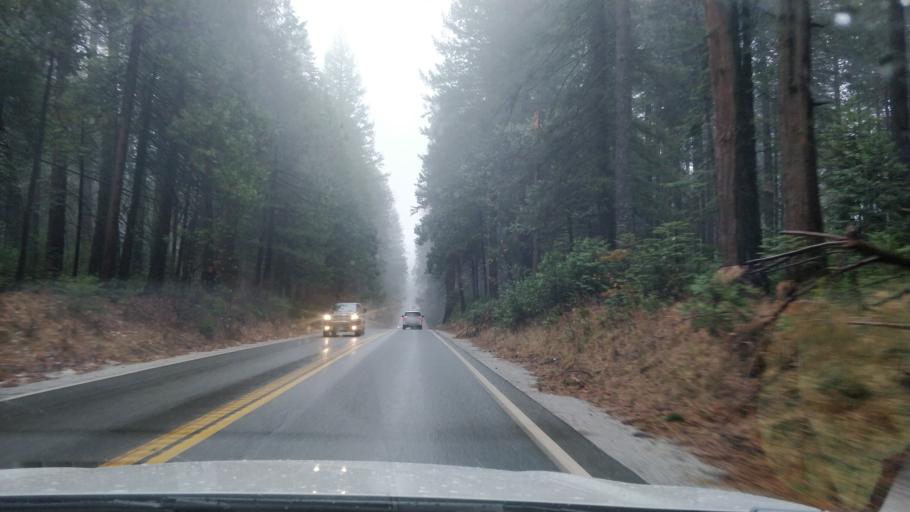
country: US
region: California
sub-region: Nevada County
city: Nevada City
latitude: 39.3229
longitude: -120.8706
